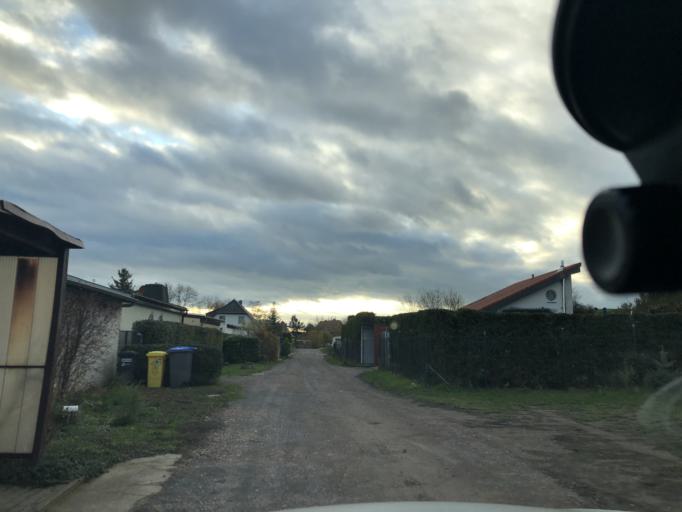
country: DE
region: Saxony-Anhalt
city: Zscherben
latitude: 51.4714
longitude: 11.8732
